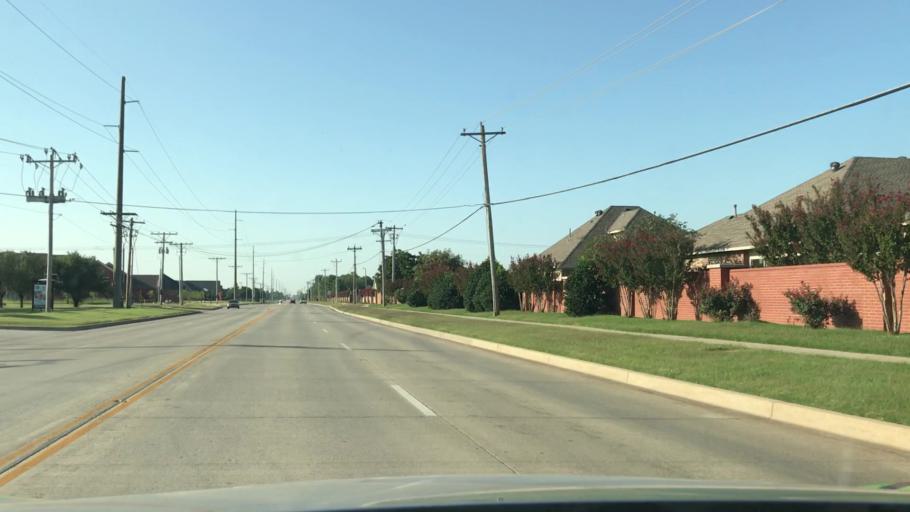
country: US
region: Oklahoma
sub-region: Cleveland County
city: Norman
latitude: 35.2558
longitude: -97.4943
